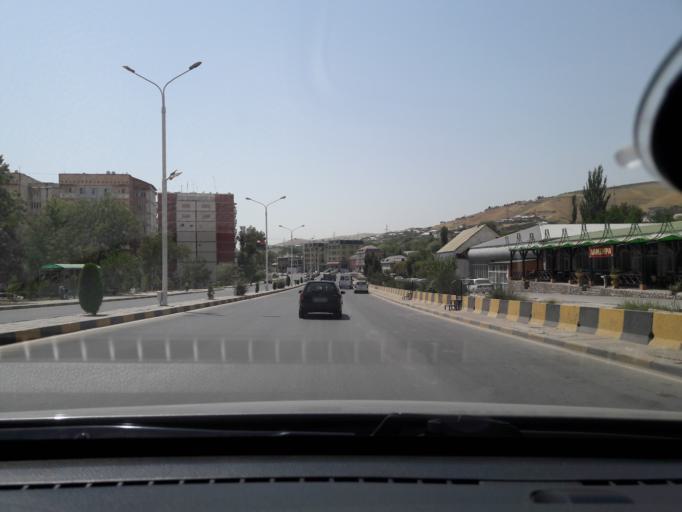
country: TJ
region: Dushanbe
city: Dushanbe
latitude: 38.5881
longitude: 68.7205
